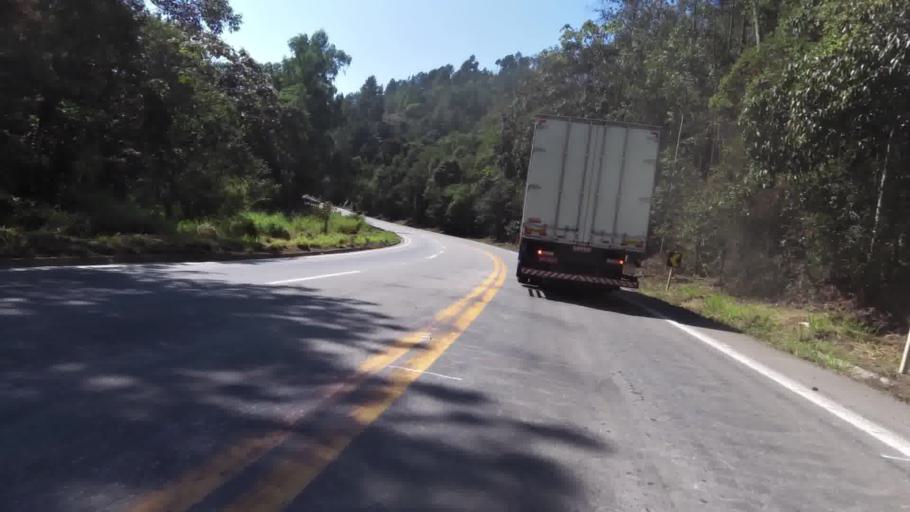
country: BR
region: Espirito Santo
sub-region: Marechal Floriano
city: Marechal Floriano
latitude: -20.4169
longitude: -40.8644
